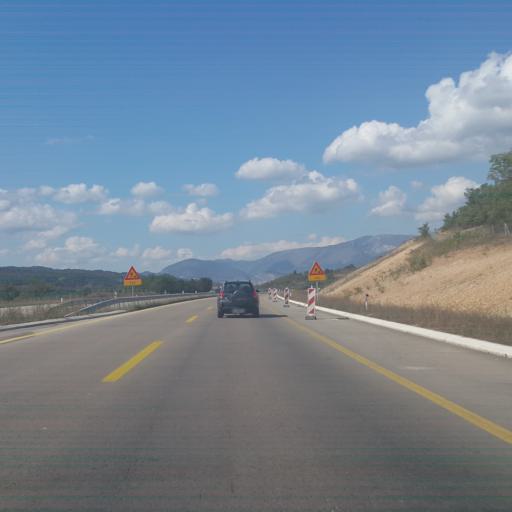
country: RS
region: Central Serbia
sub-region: Pirotski Okrug
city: Bela Palanka
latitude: 43.2408
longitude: 22.2854
